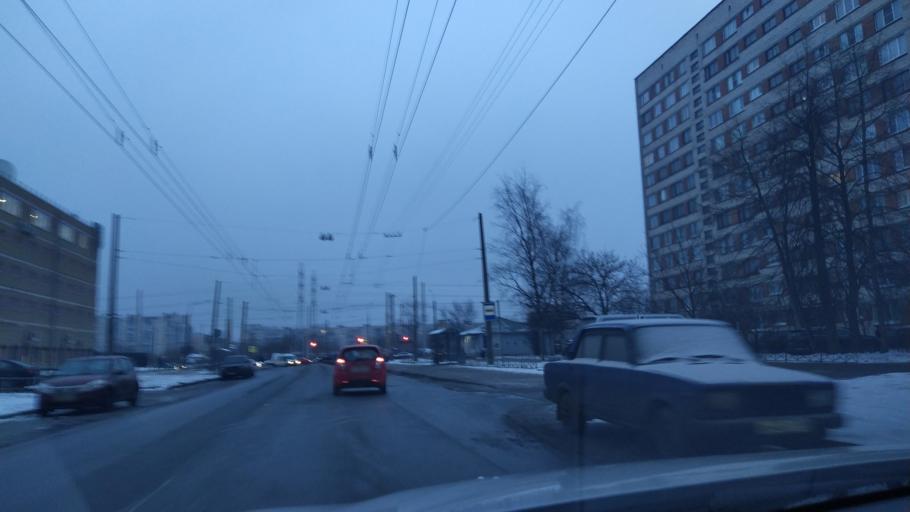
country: RU
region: St.-Petersburg
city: Grazhdanka
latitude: 60.0181
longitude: 30.4162
